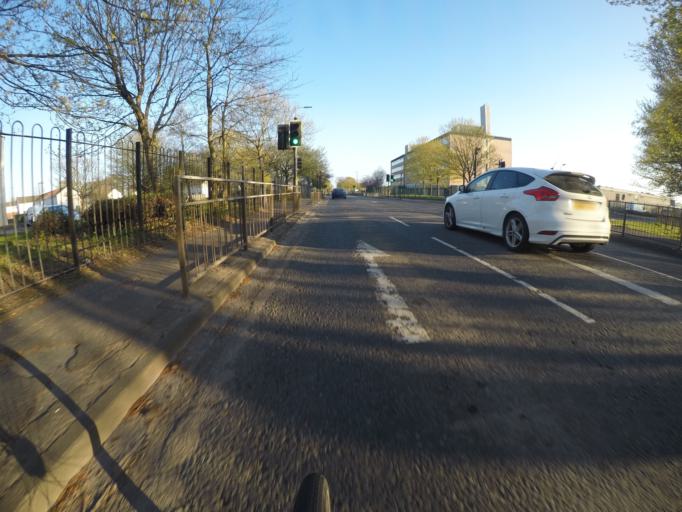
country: GB
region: Scotland
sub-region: North Ayrshire
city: Irvine
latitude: 55.6293
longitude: -4.6750
